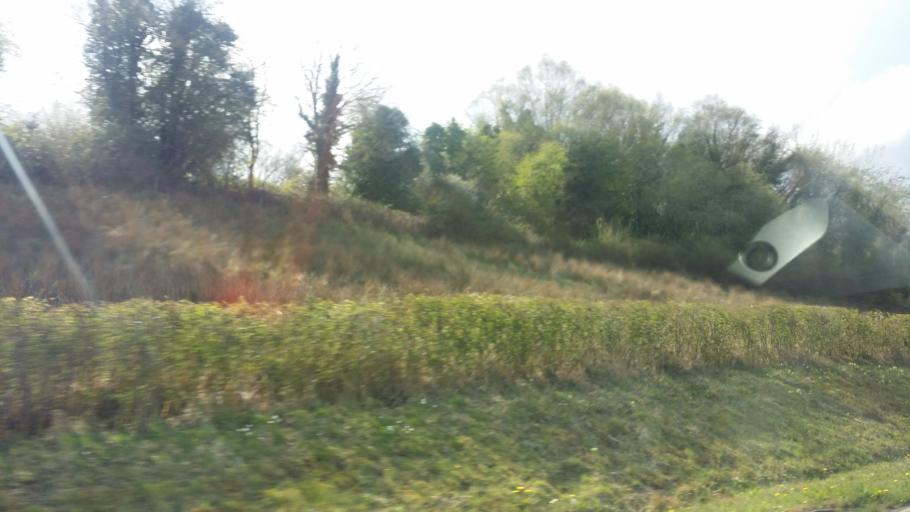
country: GB
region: Northern Ireland
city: Irvinestown
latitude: 54.4534
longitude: -7.8182
